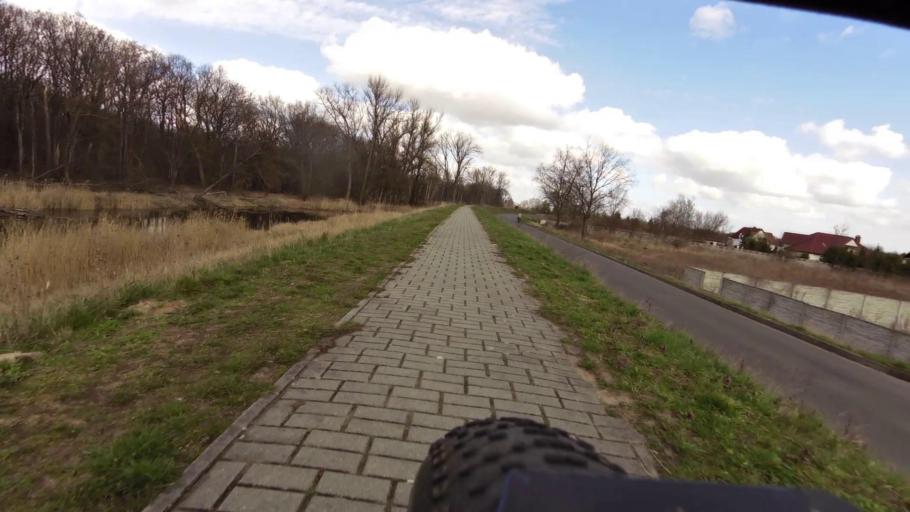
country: PL
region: Lubusz
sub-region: Powiat slubicki
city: Slubice
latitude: 52.3643
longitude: 14.5613
